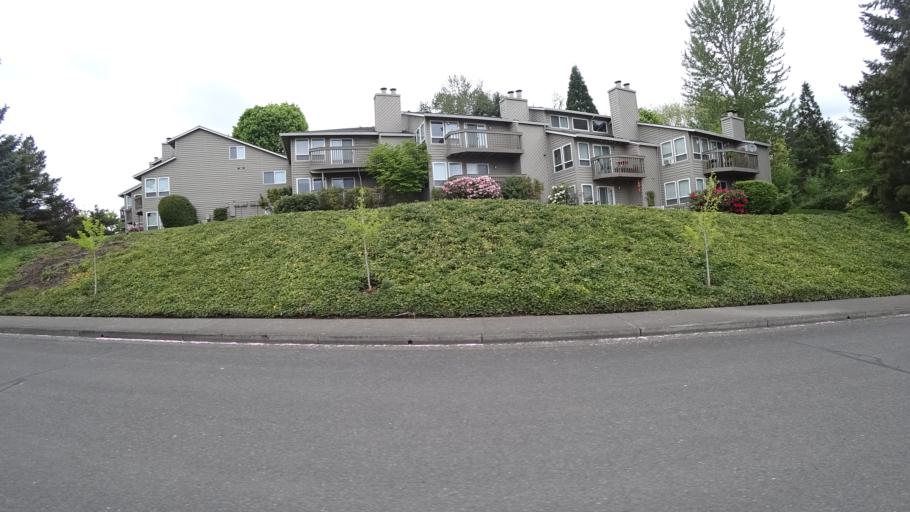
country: US
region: Oregon
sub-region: Washington County
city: Beaverton
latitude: 45.4572
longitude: -122.8227
